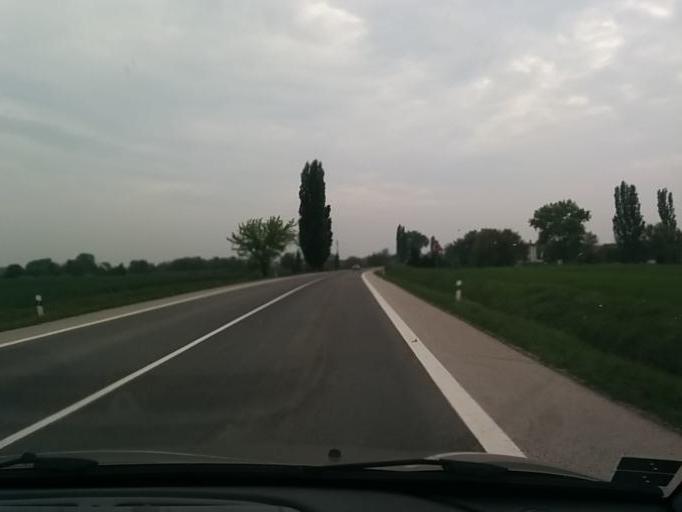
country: SK
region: Trnavsky
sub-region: Okres Galanta
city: Galanta
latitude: 48.2491
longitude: 17.7060
